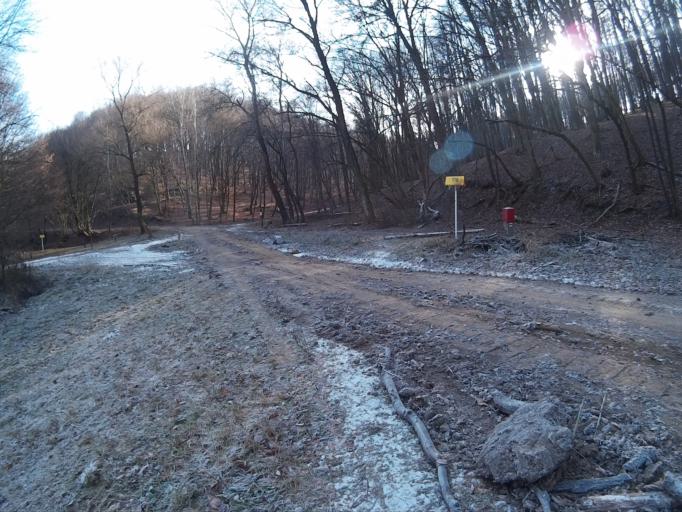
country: HU
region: Fejer
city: Szarliget
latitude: 47.5005
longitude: 18.4125
